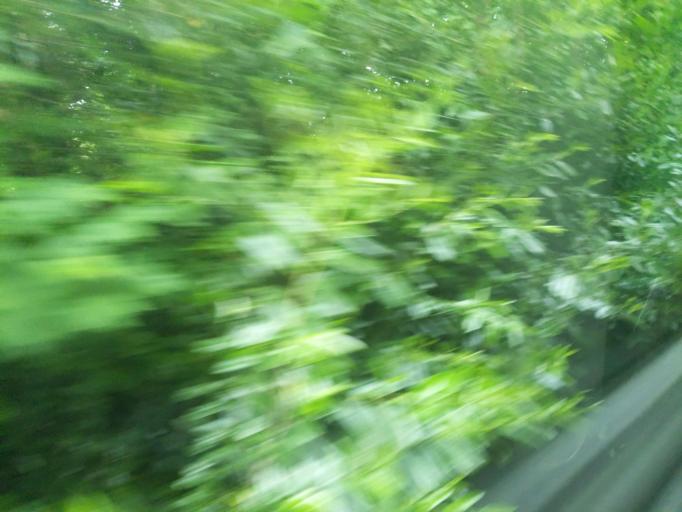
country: GB
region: England
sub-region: Devon
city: Crediton
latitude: 50.7798
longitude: -3.6246
